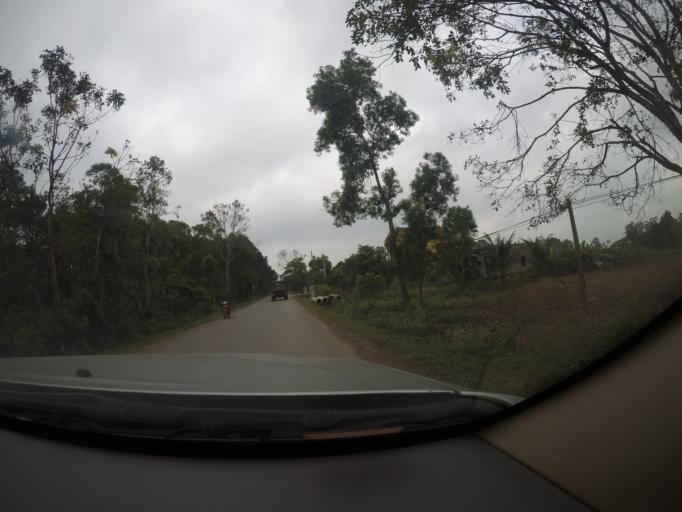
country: VN
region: Quang Binh
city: Hoan Lao
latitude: 17.6331
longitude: 106.4318
